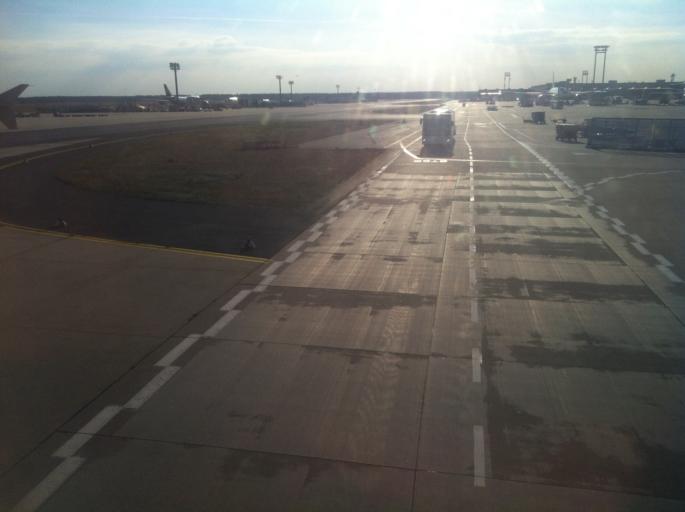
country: DE
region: Hesse
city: Kelsterbach
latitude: 50.0405
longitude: 8.5492
